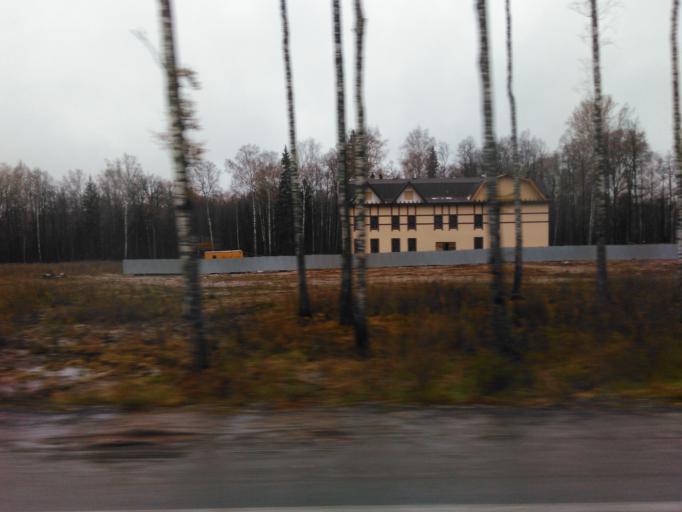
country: RU
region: Tatarstan
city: Osinovo
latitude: 55.8474
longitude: 48.8525
